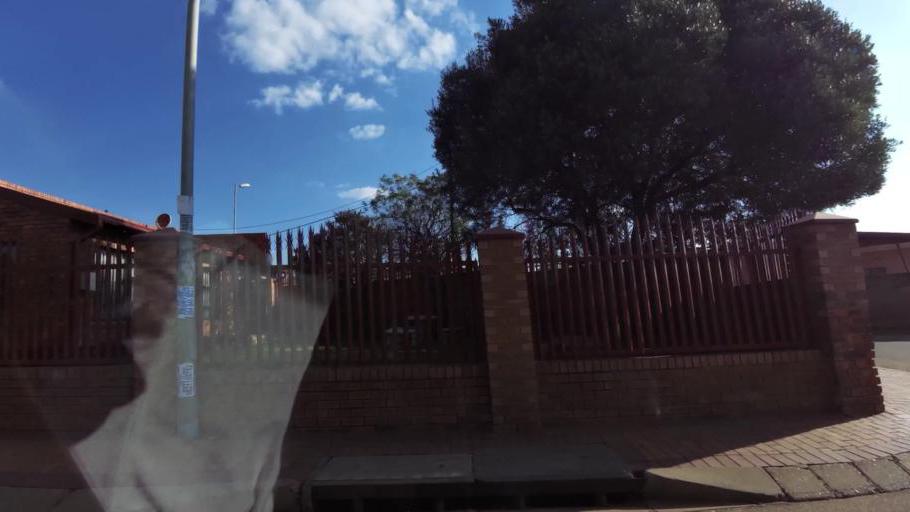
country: ZA
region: Gauteng
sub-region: City of Johannesburg Metropolitan Municipality
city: Soweto
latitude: -26.2276
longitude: 27.8733
